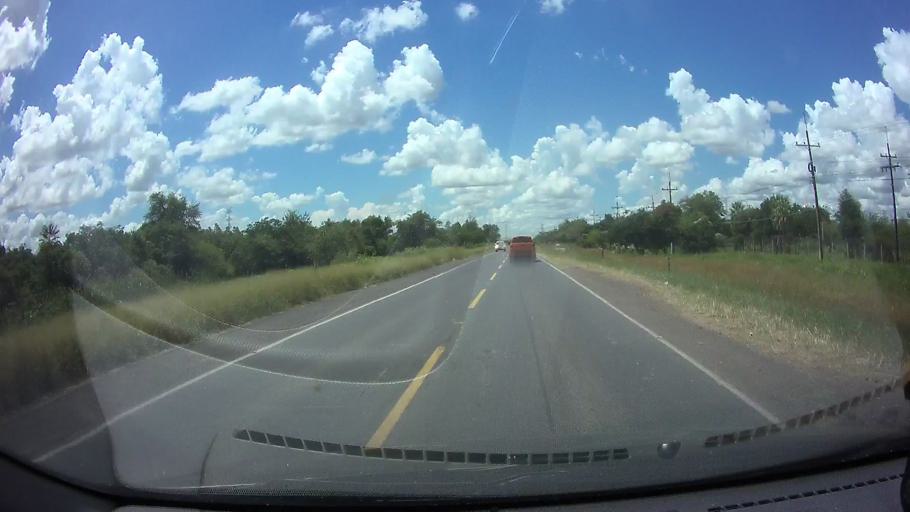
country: PY
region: Central
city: Colonia Mariano Roque Alonso
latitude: -25.1837
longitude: -57.5914
